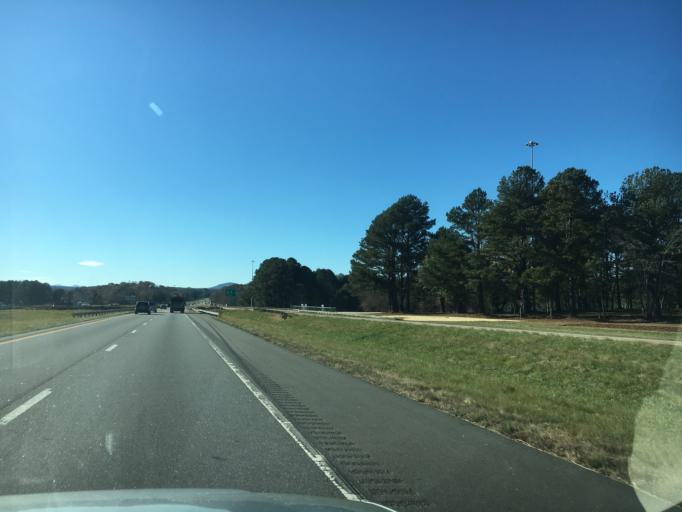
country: US
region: North Carolina
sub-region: Catawba County
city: Hickory
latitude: 35.7087
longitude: -81.3509
